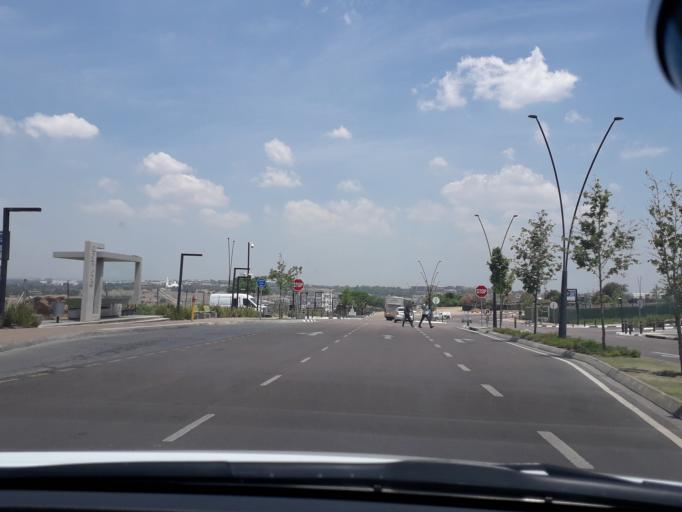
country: ZA
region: Gauteng
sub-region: City of Johannesburg Metropolitan Municipality
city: Midrand
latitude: -26.0172
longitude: 28.1086
